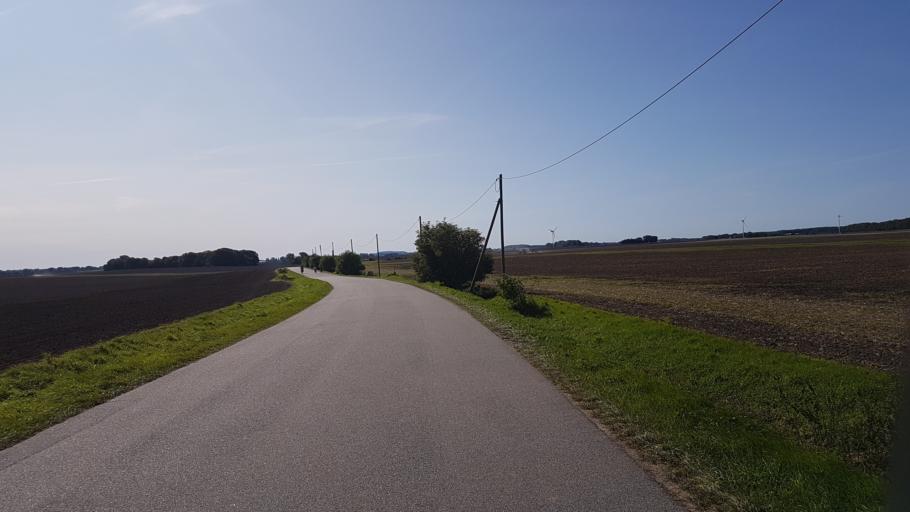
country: DE
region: Mecklenburg-Vorpommern
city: Altenkirchen
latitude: 54.6631
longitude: 13.3515
